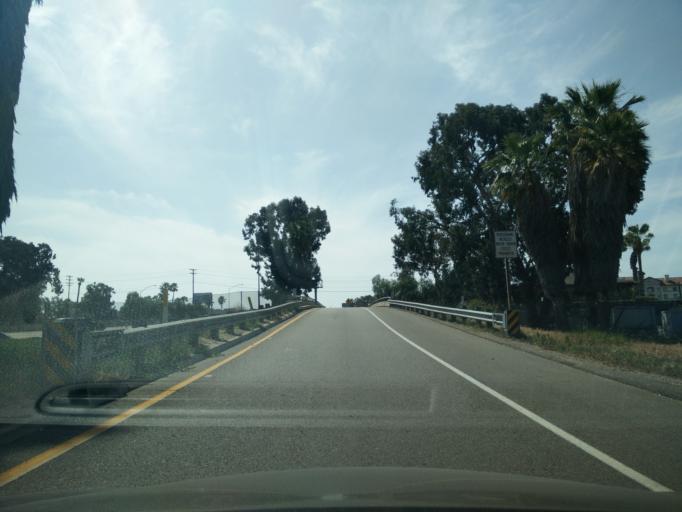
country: US
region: California
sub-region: San Diego County
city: San Diego
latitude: 32.7087
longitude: -117.1484
